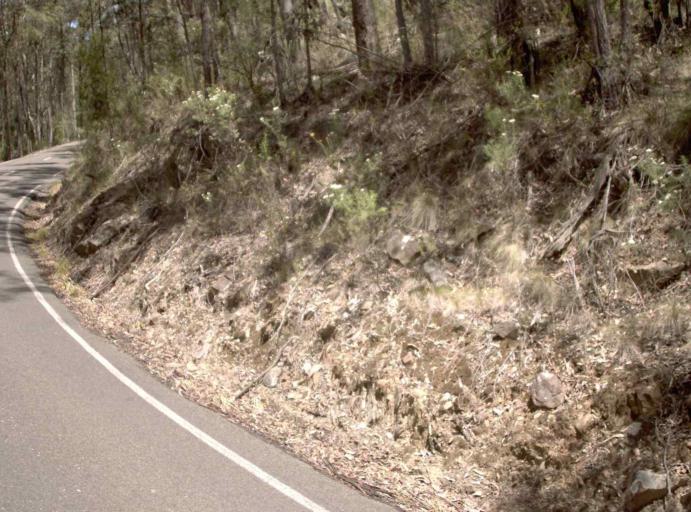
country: AU
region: Victoria
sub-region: East Gippsland
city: Lakes Entrance
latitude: -37.6003
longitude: 147.8885
